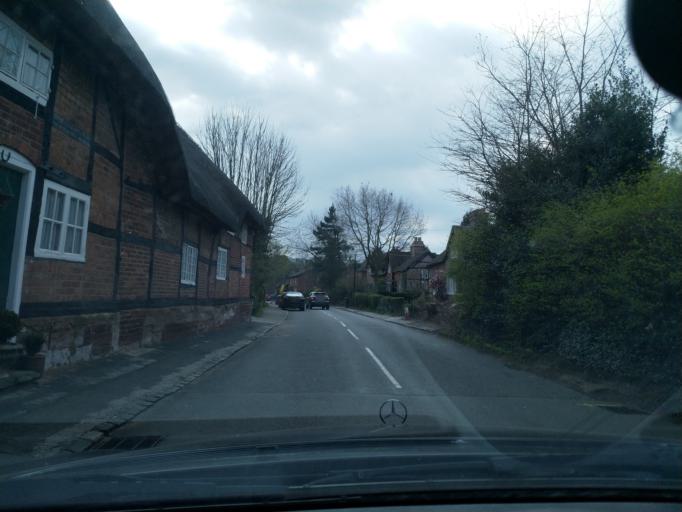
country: GB
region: England
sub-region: Coventry
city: Coventry
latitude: 52.3531
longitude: -1.5194
